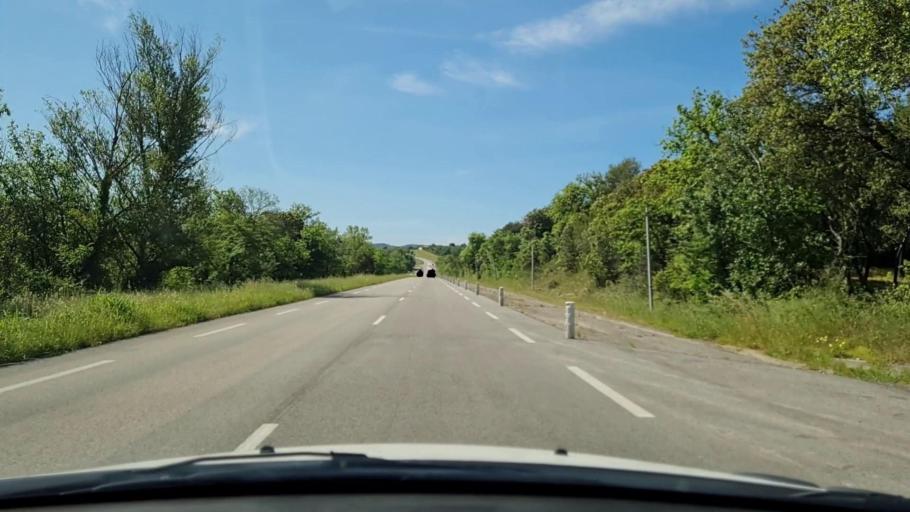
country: FR
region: Languedoc-Roussillon
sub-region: Departement du Gard
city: Vezenobres
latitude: 44.0365
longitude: 4.1485
